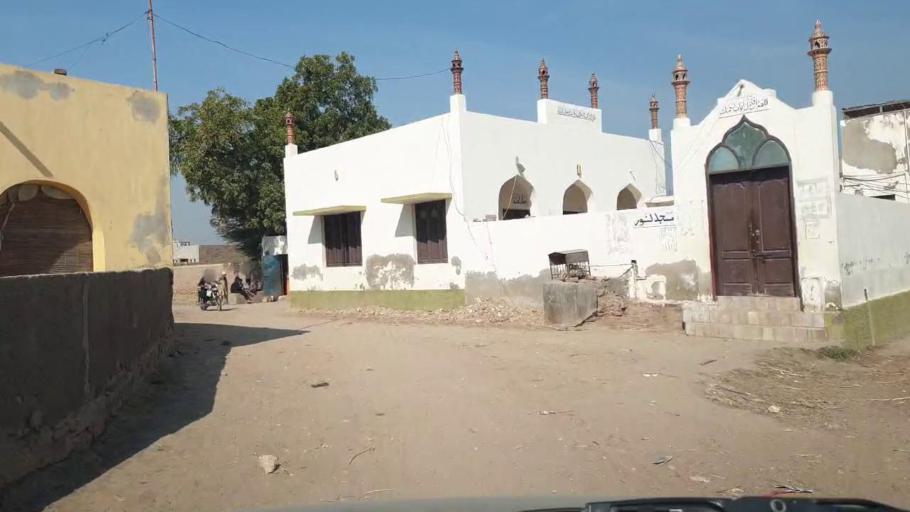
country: PK
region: Sindh
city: Tando Allahyar
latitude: 25.4041
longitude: 68.7437
